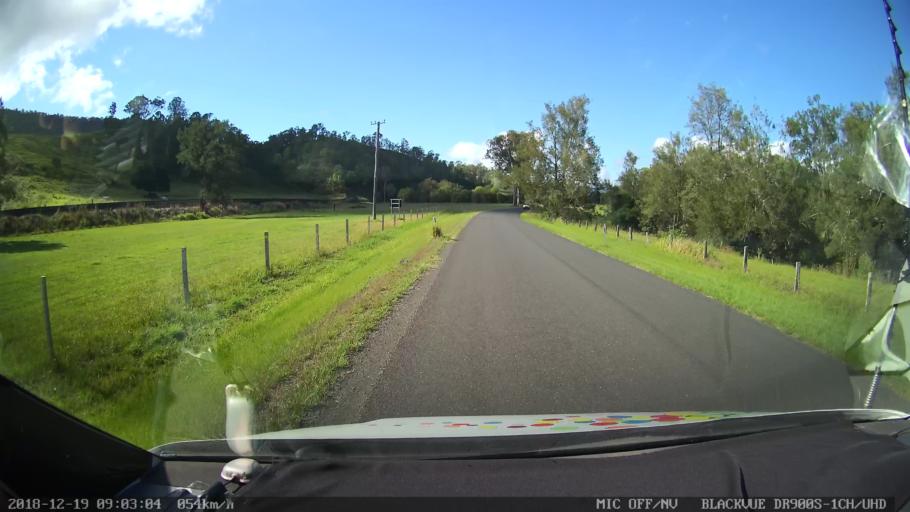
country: AU
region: New South Wales
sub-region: Kyogle
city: Kyogle
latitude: -28.4445
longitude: 152.9523
